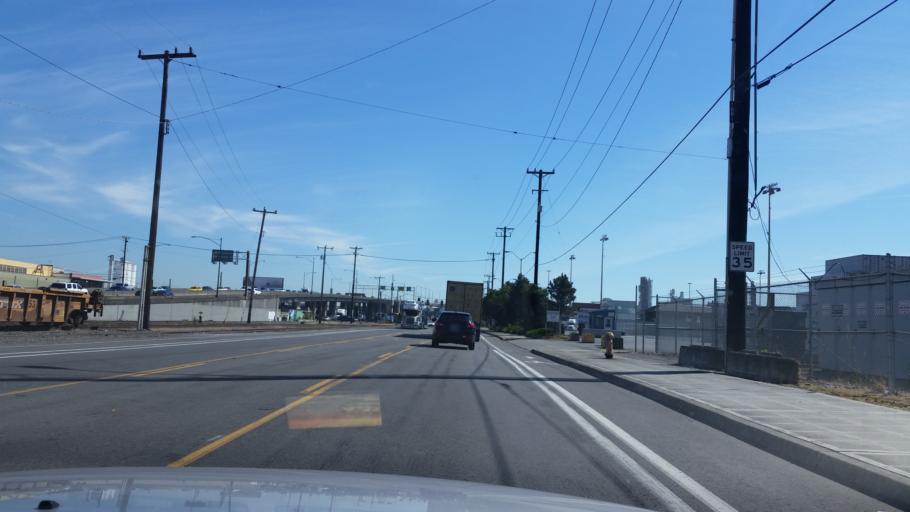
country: US
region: Washington
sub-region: King County
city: Seattle
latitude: 47.5774
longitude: -122.3401
